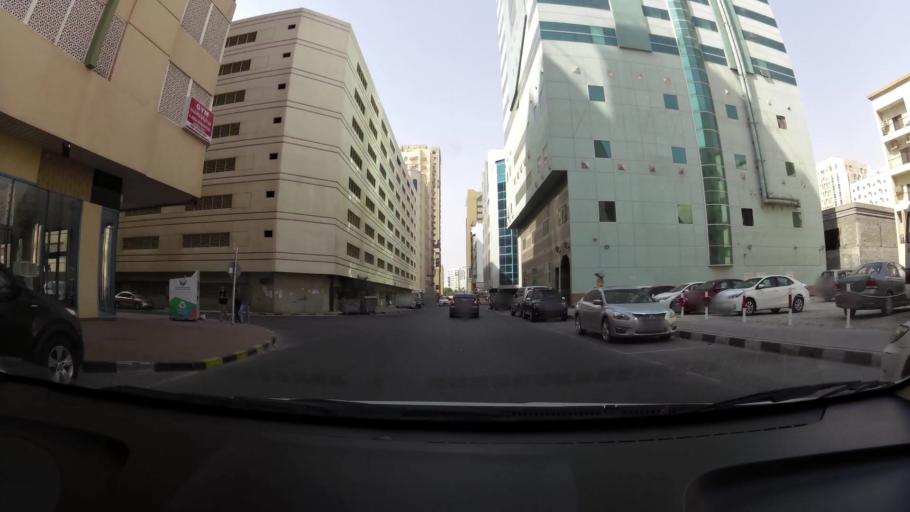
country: AE
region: Ash Shariqah
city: Sharjah
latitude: 25.3410
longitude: 55.3934
